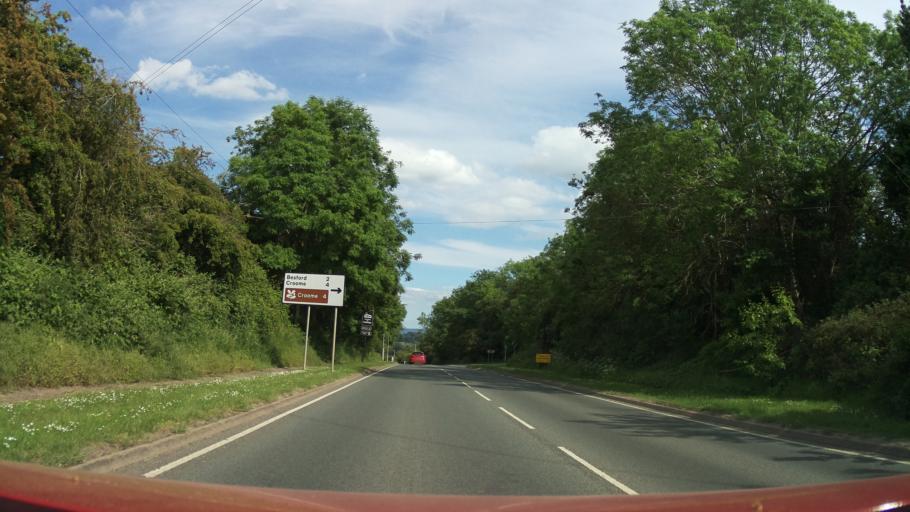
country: GB
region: England
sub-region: Worcestershire
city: Pershore
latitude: 52.1155
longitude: -2.0905
